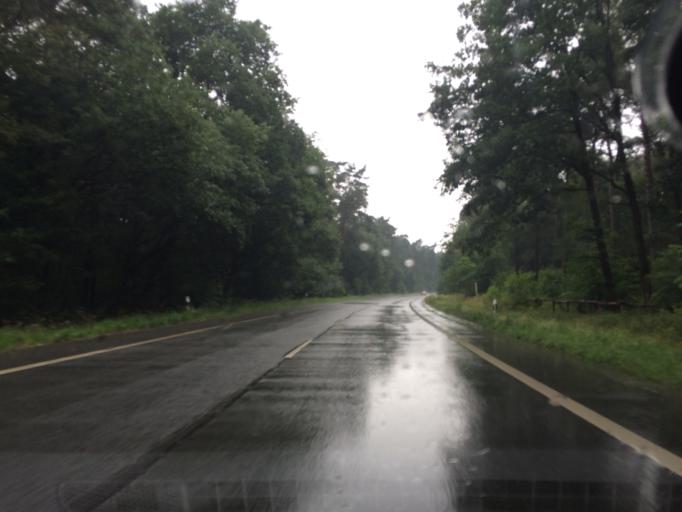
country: DE
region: North Rhine-Westphalia
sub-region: Regierungsbezirk Munster
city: Haltern
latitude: 51.7601
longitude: 7.2362
